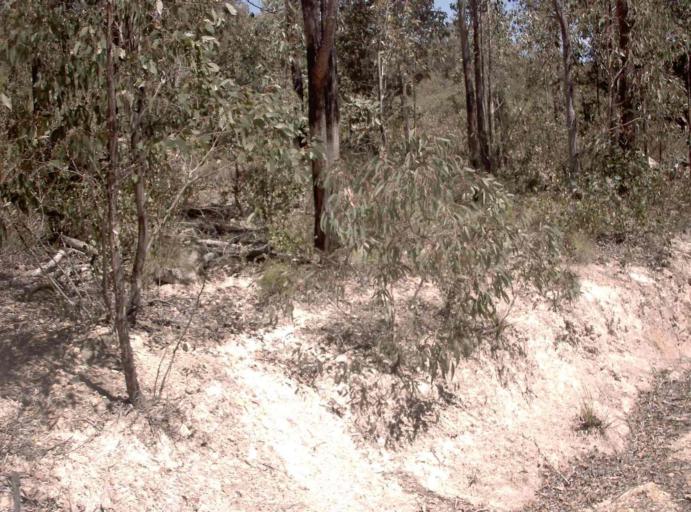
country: AU
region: New South Wales
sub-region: Snowy River
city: Jindabyne
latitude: -37.1217
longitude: 148.2468
